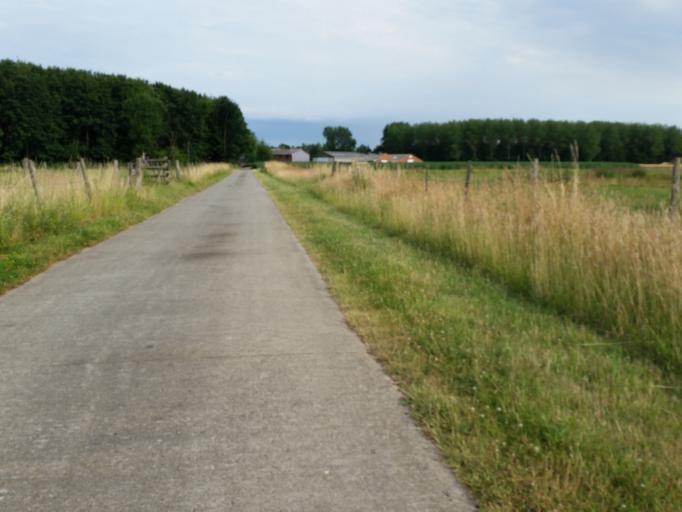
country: BE
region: Flanders
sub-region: Provincie Vlaams-Brabant
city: Zemst
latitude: 50.9822
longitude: 4.4896
